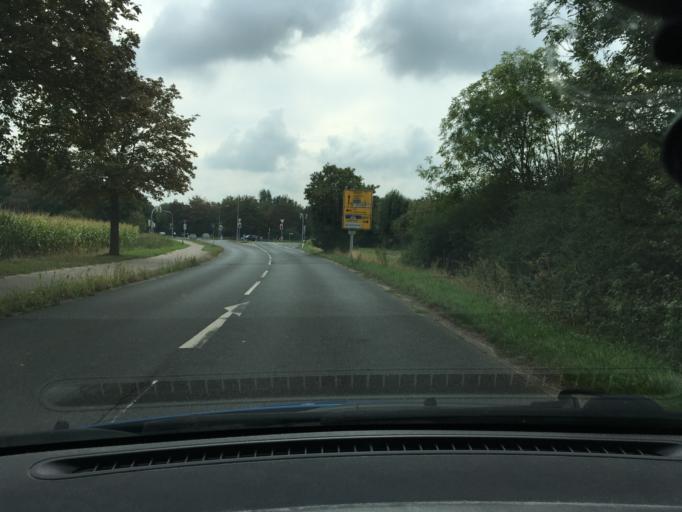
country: DE
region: Lower Saxony
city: Garbsen
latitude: 52.4330
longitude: 9.5747
